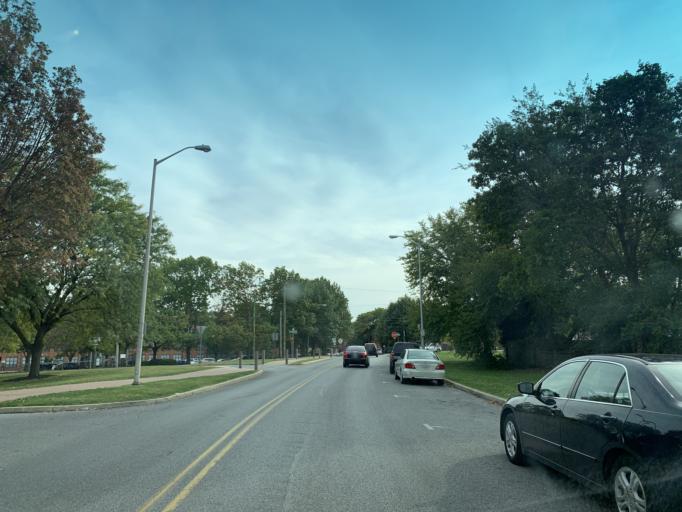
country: US
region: Pennsylvania
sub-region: York County
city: York
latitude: 39.9628
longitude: -76.7183
